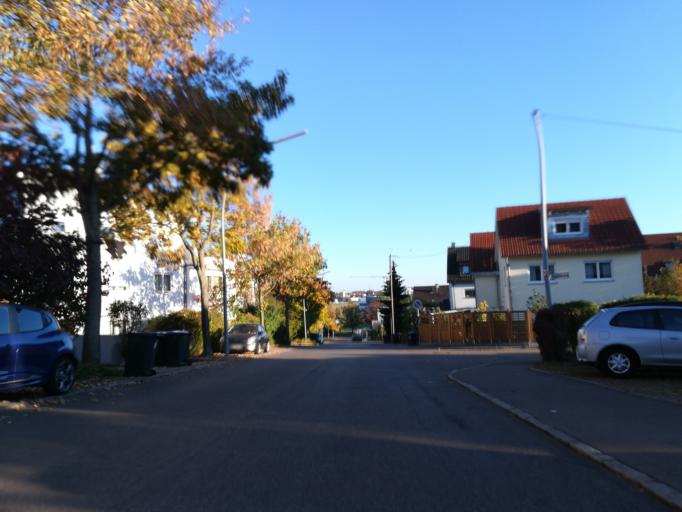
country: DE
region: Baden-Wuerttemberg
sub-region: Regierungsbezirk Stuttgart
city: Filderstadt
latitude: 48.6766
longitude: 9.2264
